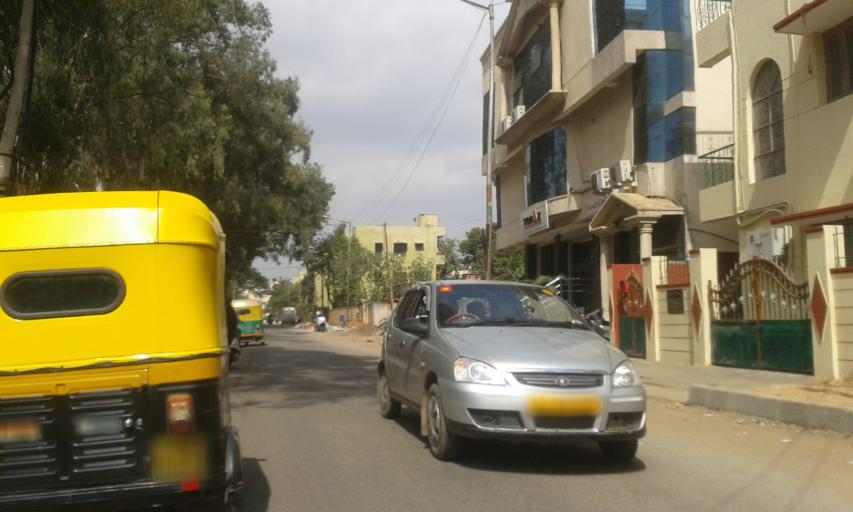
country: IN
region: Karnataka
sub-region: Bangalore Urban
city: Bangalore
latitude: 12.9589
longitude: 77.6122
